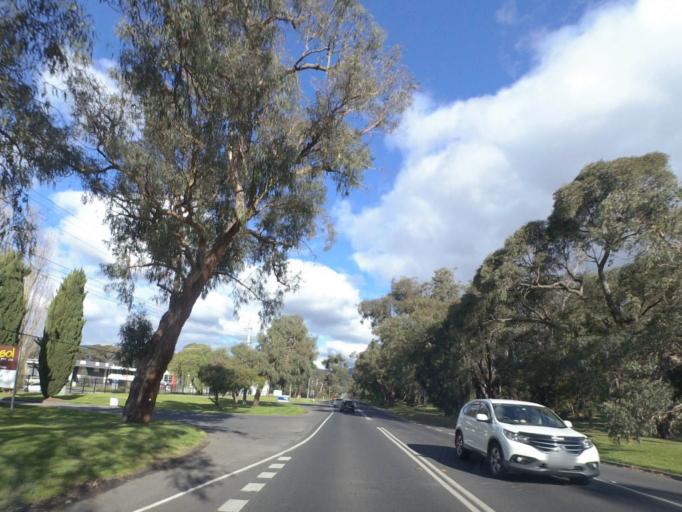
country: AU
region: Victoria
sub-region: Maroondah
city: Bayswater North
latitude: -37.8392
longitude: 145.2944
